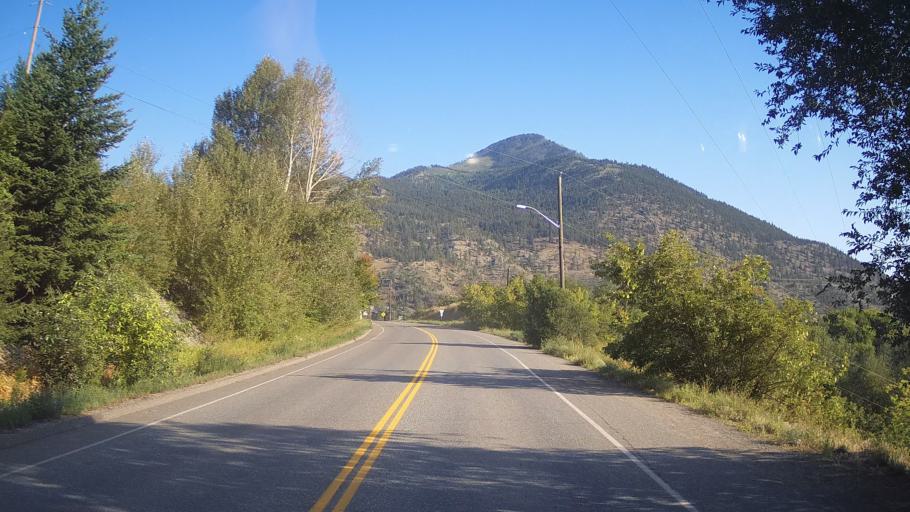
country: CA
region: British Columbia
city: Lillooet
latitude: 50.6835
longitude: -121.9334
